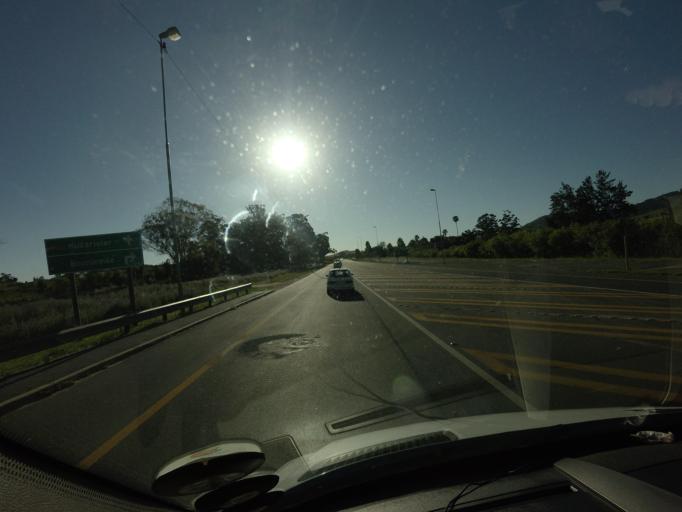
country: ZA
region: Western Cape
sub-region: Cape Winelands District Municipality
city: Stellenbosch
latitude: -33.9534
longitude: 18.7959
